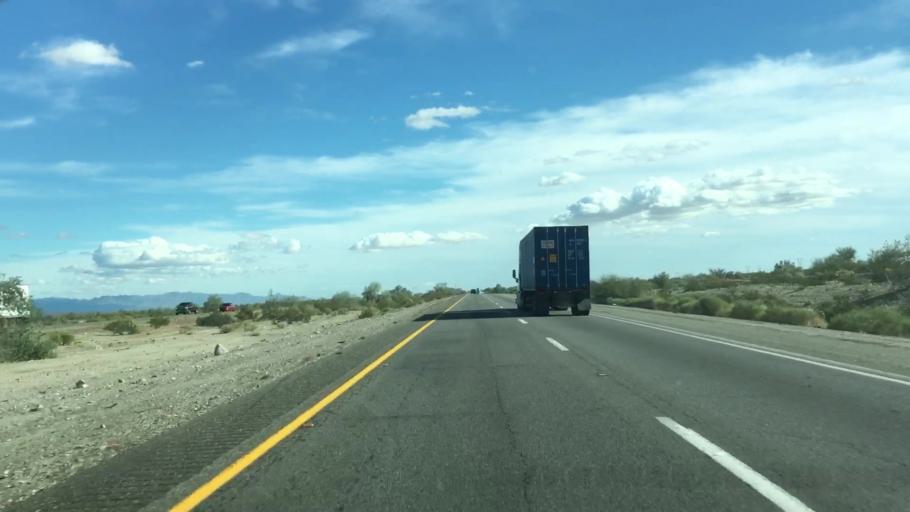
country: US
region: California
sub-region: Imperial County
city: Niland
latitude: 33.6978
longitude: -115.2962
